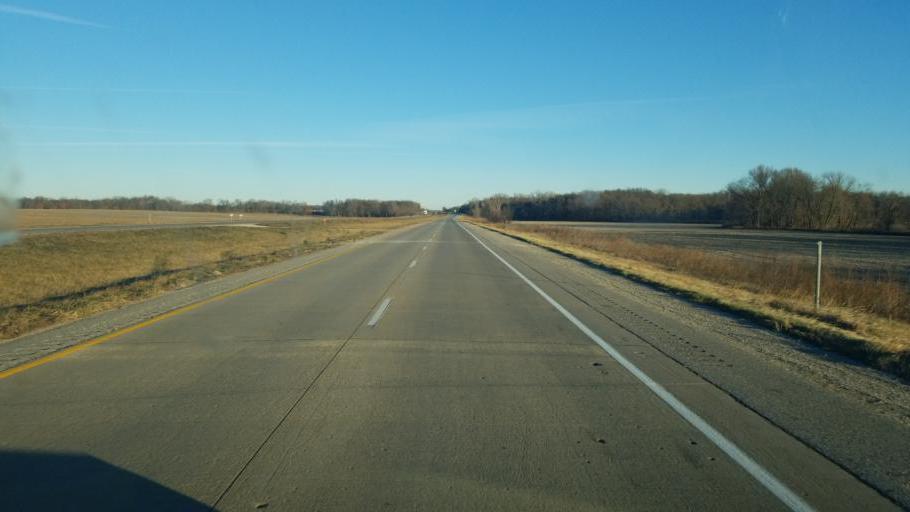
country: US
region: Iowa
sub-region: Wapello County
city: Eddyville
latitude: 41.1936
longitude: -92.6400
